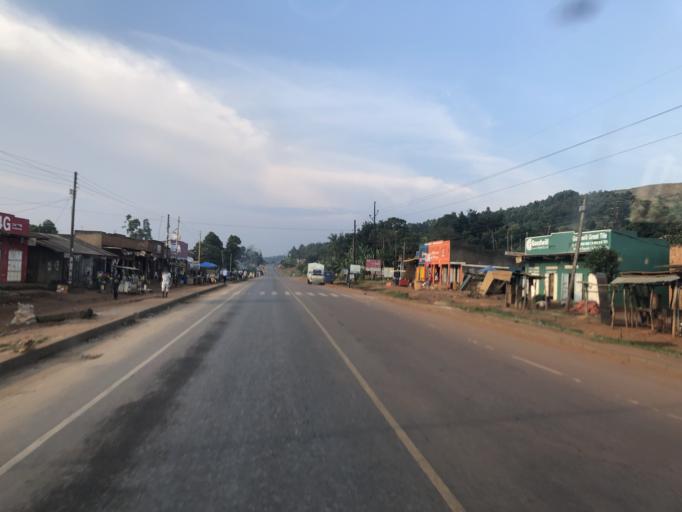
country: UG
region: Central Region
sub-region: Mpigi District
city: Mpigi
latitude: 0.1919
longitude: 32.2949
